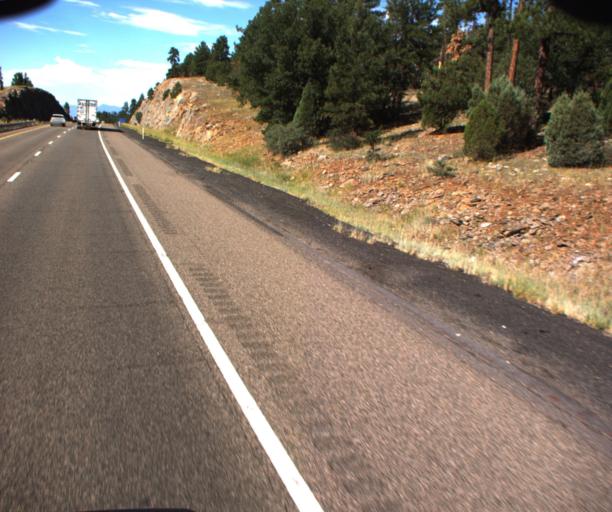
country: US
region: Arizona
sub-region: Coconino County
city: Sedona
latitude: 34.8281
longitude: -111.6090
